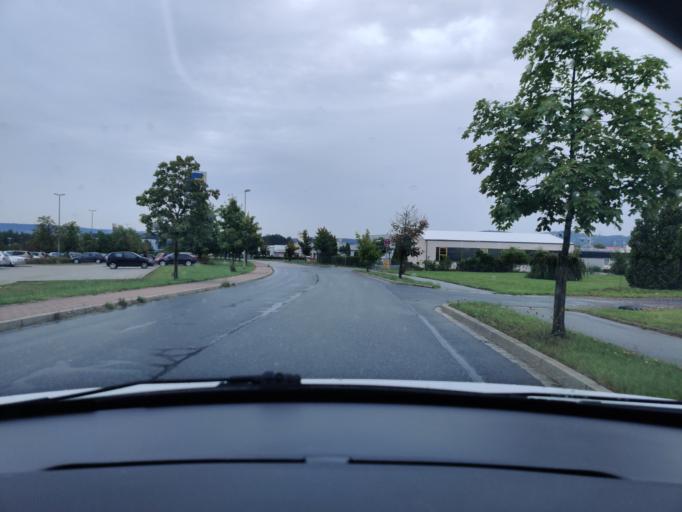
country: DE
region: Bavaria
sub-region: Upper Palatinate
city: Wernberg-Koblitz
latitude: 49.5284
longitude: 12.1401
